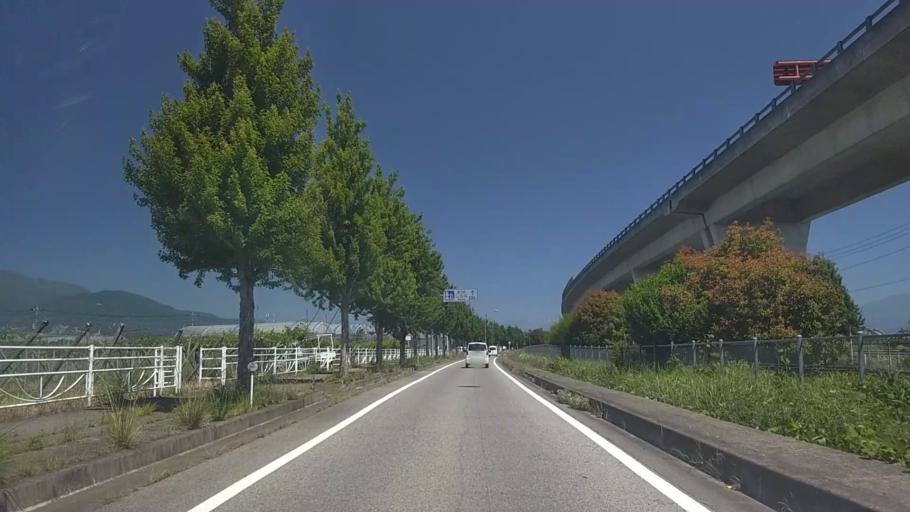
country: JP
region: Yamanashi
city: Ryuo
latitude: 35.6328
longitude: 138.4723
